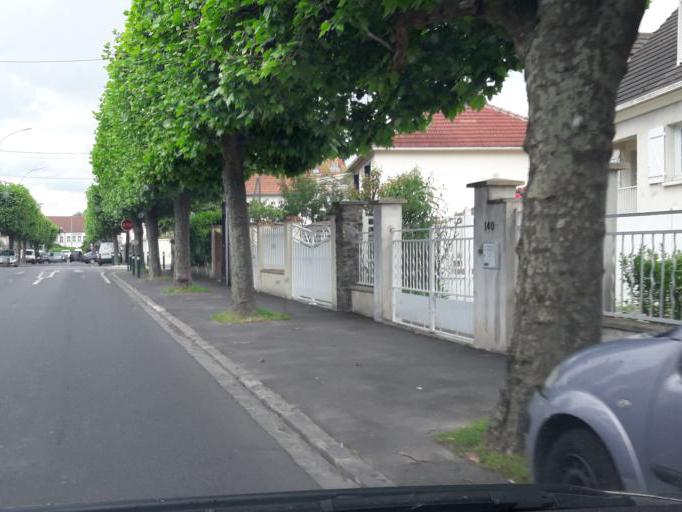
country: FR
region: Ile-de-France
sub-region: Departement de l'Essonne
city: Sainte-Genevieve-des-Bois
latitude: 48.6440
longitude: 2.3327
